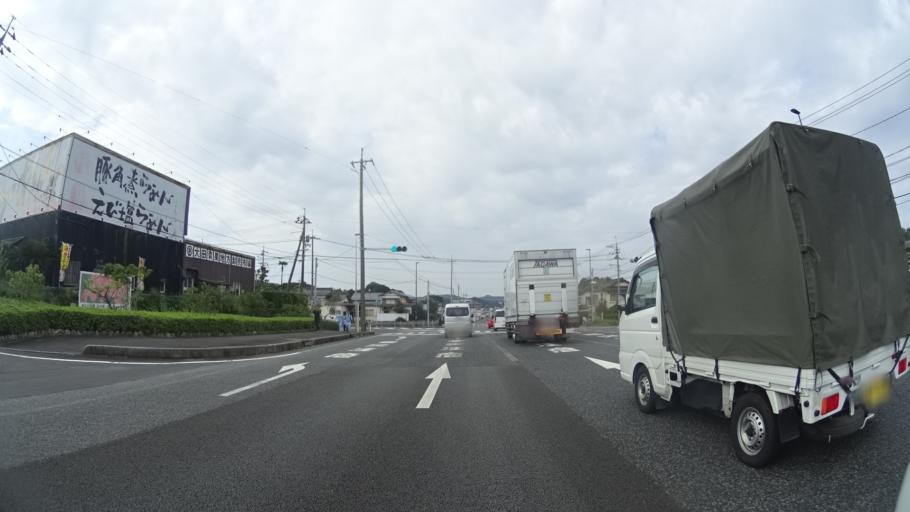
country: JP
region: Shimane
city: Odacho-oda
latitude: 35.2050
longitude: 132.5009
